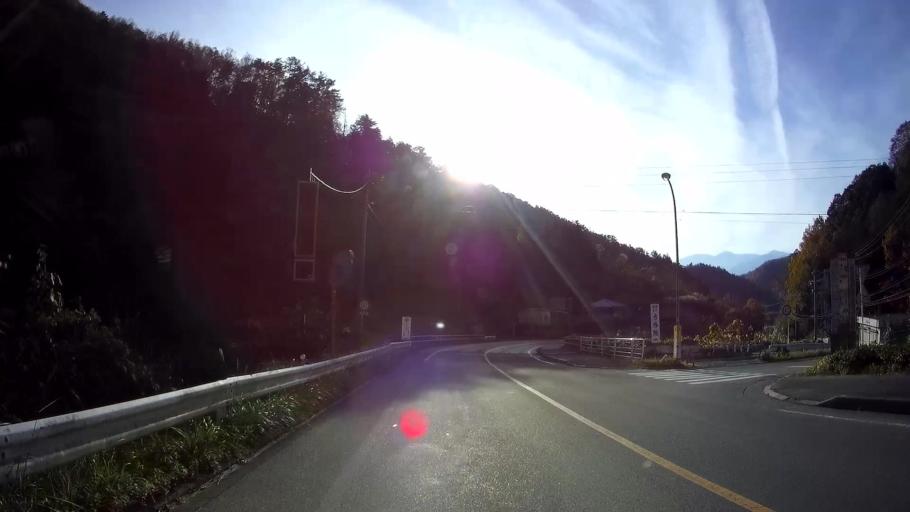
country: JP
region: Yamanashi
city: Fujikawaguchiko
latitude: 35.4742
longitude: 138.5350
